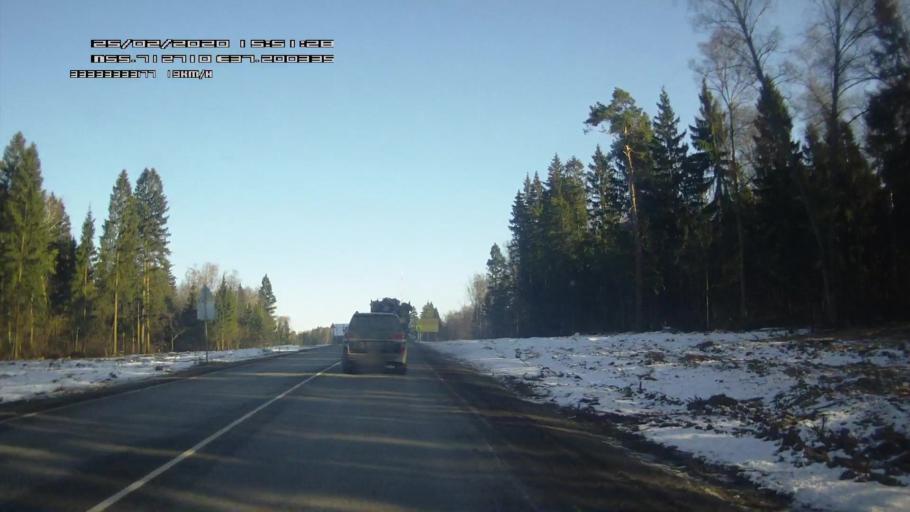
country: RU
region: Moskovskaya
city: Gorki Vtoryye
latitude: 55.7128
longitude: 37.2000
